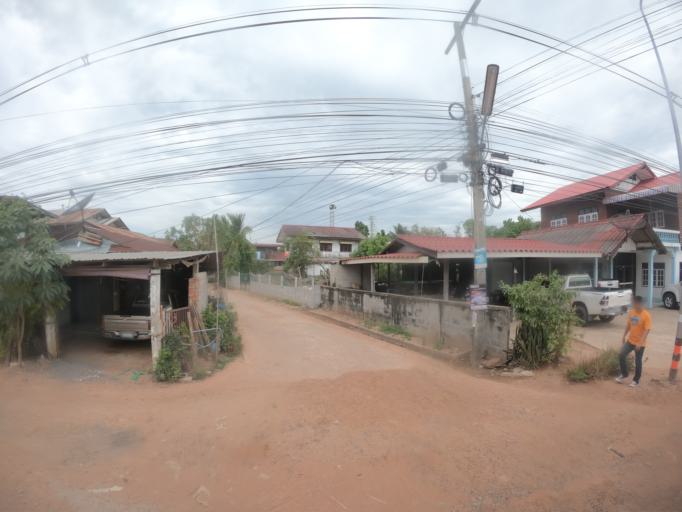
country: TH
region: Maha Sarakham
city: Kantharawichai
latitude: 16.3377
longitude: 103.1901
